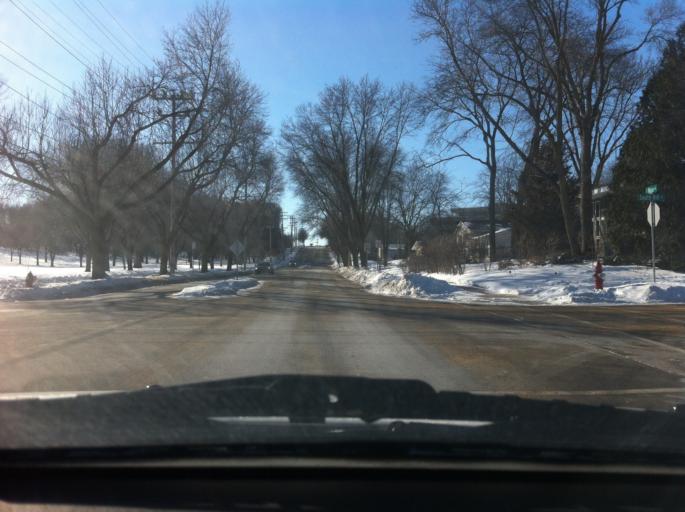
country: US
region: Wisconsin
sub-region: Dane County
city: Shorewood Hills
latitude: 43.0645
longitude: -89.4785
